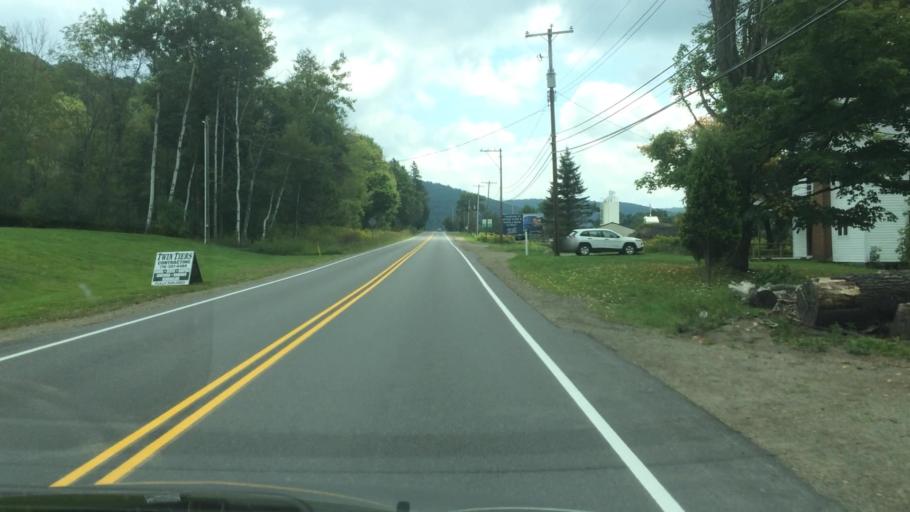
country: US
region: Pennsylvania
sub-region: McKean County
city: Bradford
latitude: 41.9091
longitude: -78.6291
